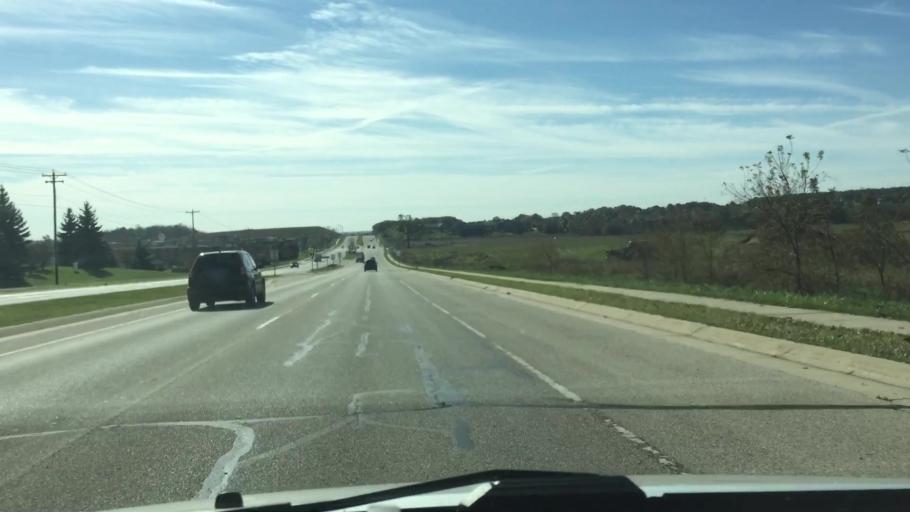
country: US
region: Wisconsin
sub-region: Waukesha County
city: Sussex
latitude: 43.1181
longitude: -88.2446
